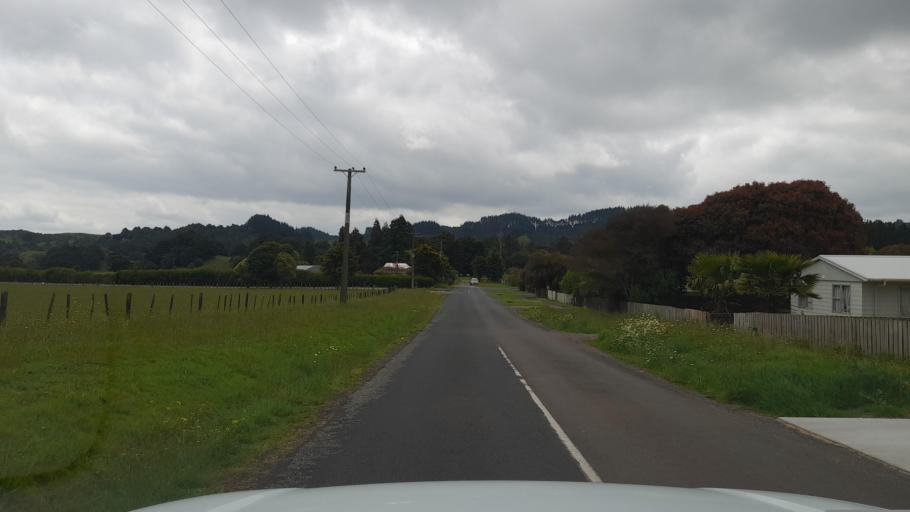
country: NZ
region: Northland
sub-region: Far North District
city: Waimate North
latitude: -35.4059
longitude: 173.7848
